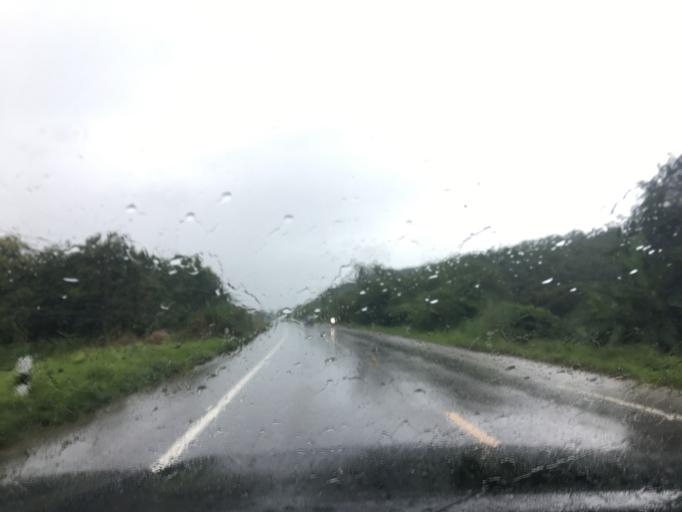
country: TH
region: Chiang Rai
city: Chiang Saen
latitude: 20.2707
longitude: 100.1962
